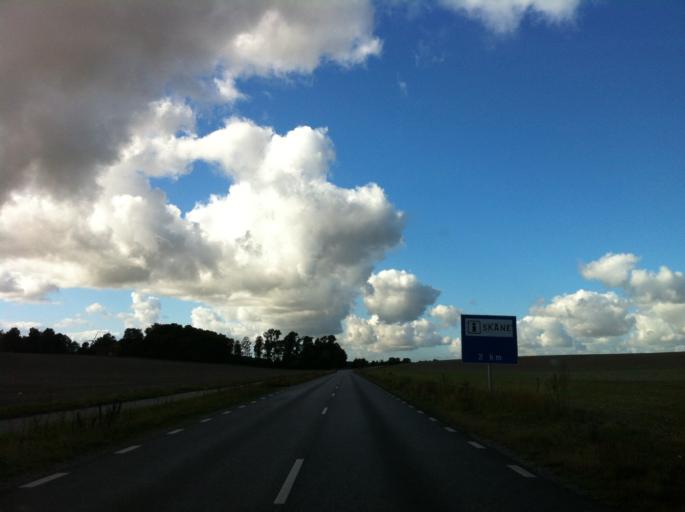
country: SE
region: Skane
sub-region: Eslovs Kommun
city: Eslov
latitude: 55.7580
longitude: 13.3365
